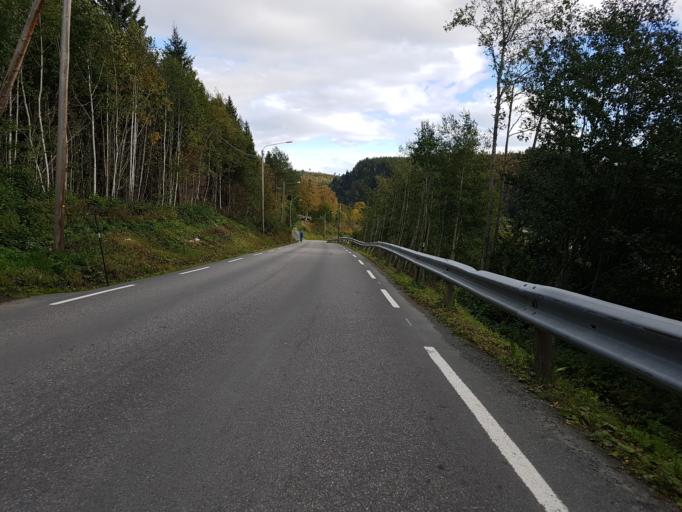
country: NO
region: Sor-Trondelag
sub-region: Klaebu
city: Klaebu
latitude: 63.3973
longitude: 10.5401
